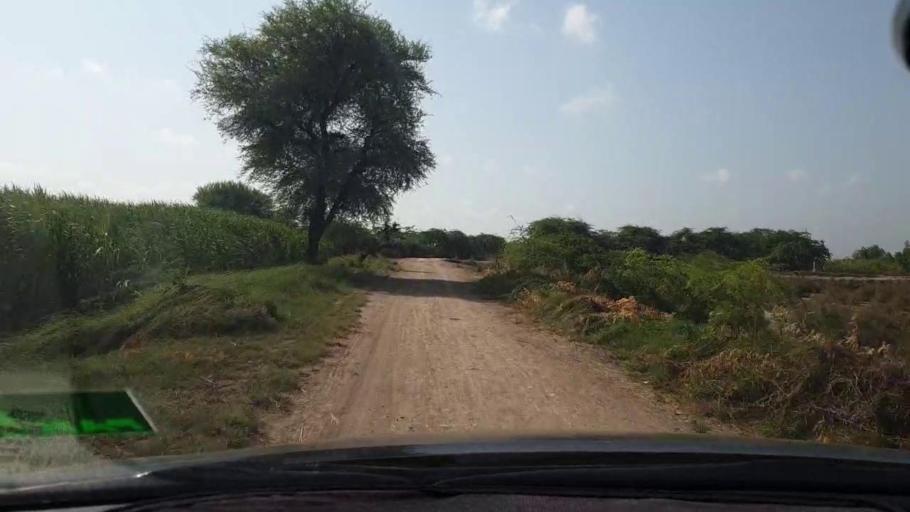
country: PK
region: Sindh
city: Tando Bago
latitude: 24.8767
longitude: 69.0107
